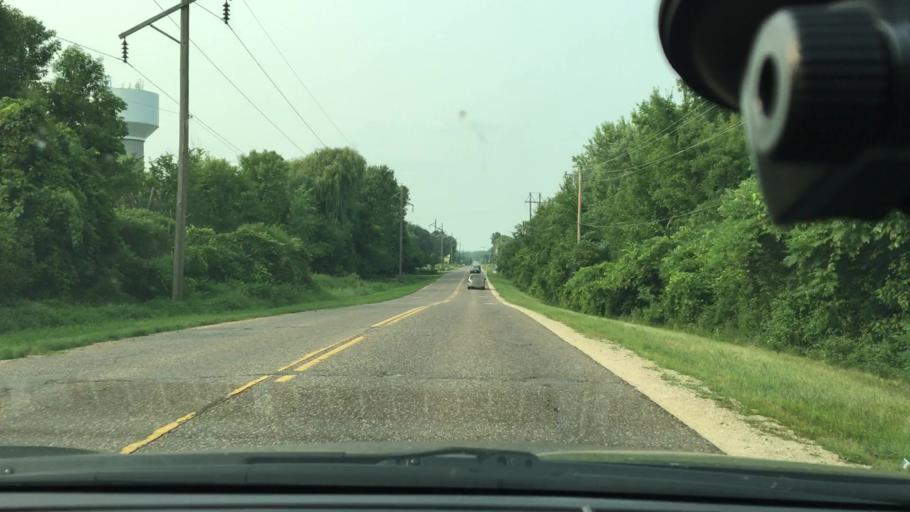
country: US
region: Minnesota
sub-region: Hennepin County
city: Champlin
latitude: 45.1901
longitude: -93.4424
